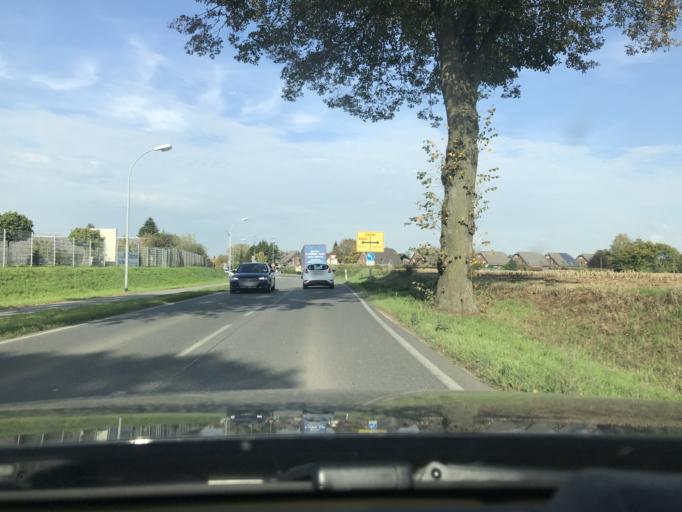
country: DE
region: North Rhine-Westphalia
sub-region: Regierungsbezirk Dusseldorf
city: Uedem
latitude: 51.6601
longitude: 6.2763
